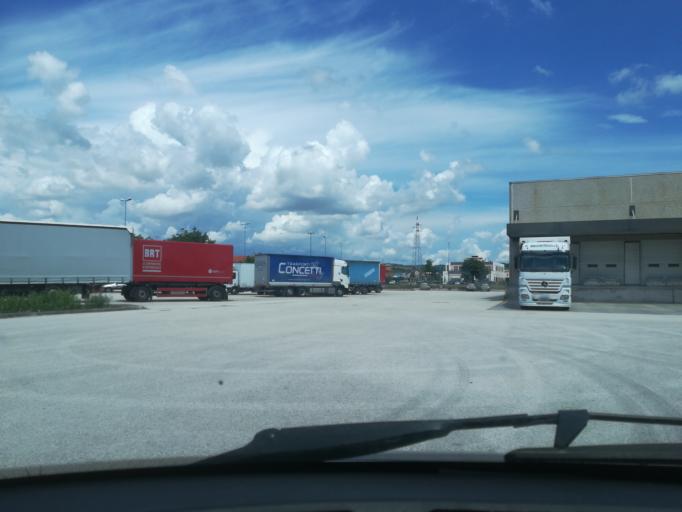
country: IT
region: The Marches
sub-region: Provincia di Macerata
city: Santa Maria Apparente
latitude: 43.2823
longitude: 13.6855
